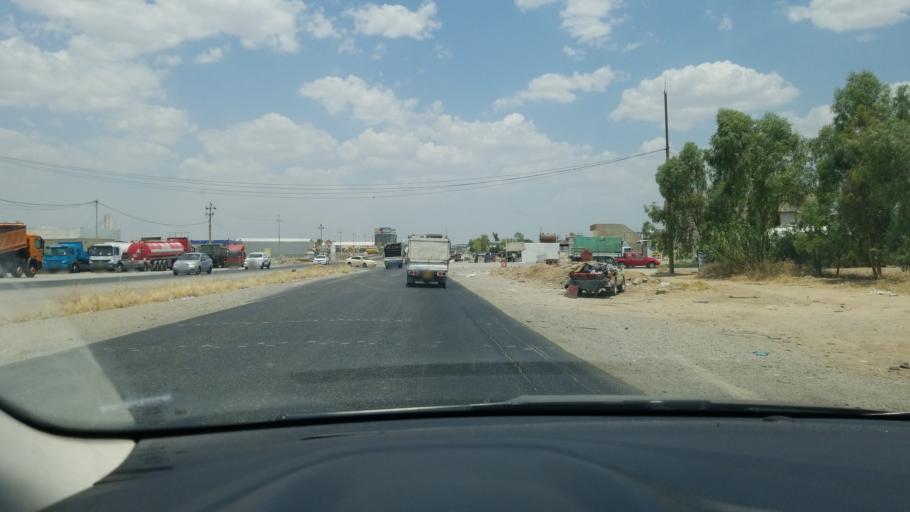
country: IQ
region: Arbil
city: Erbil
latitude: 36.0955
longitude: 44.0217
